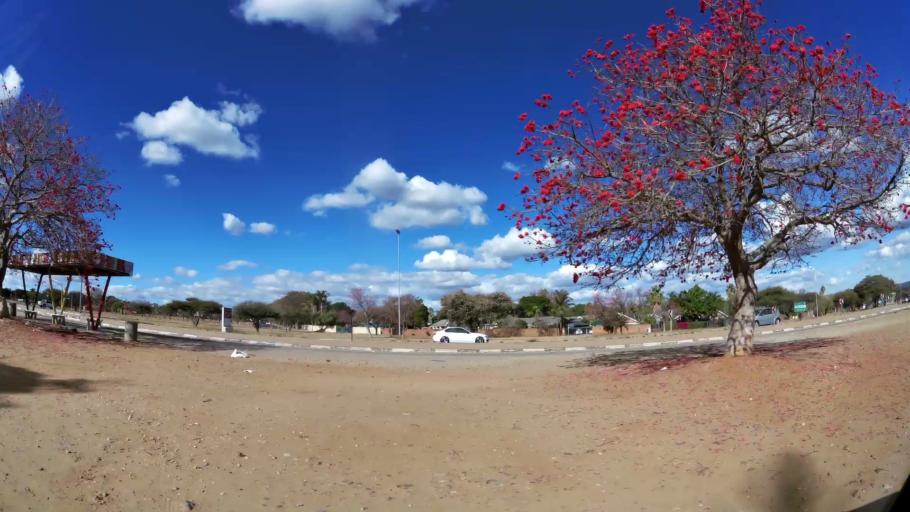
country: ZA
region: Limpopo
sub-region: Capricorn District Municipality
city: Polokwane
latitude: -23.9003
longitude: 29.4785
